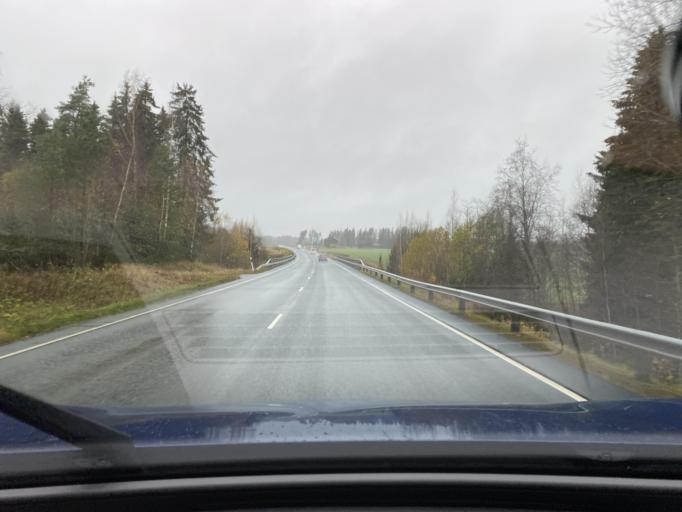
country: FI
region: Varsinais-Suomi
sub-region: Loimaa
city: Alastaro
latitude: 60.9320
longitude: 22.8731
